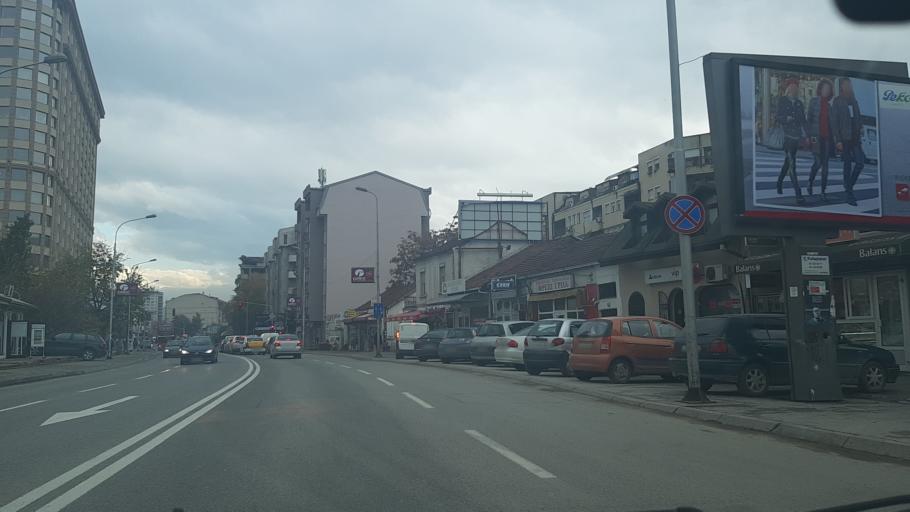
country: MK
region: Karpos
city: Skopje
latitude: 41.9865
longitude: 21.4372
